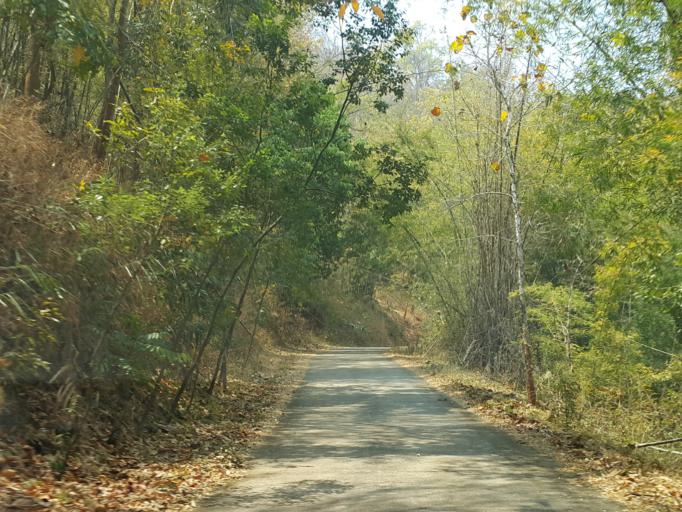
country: TH
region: Chiang Mai
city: Samoeng
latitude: 18.7999
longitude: 98.8083
